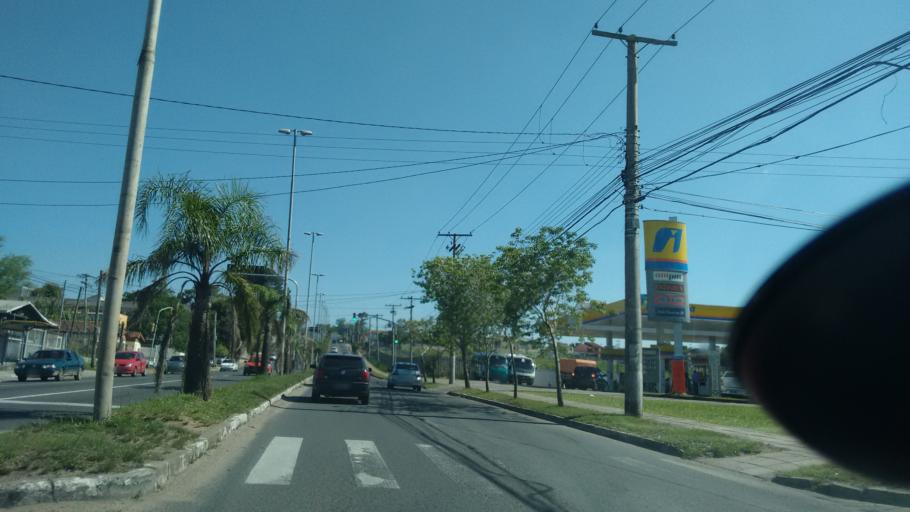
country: BR
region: Rio Grande do Sul
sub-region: Cachoeirinha
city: Cachoeirinha
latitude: -30.0199
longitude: -51.1197
